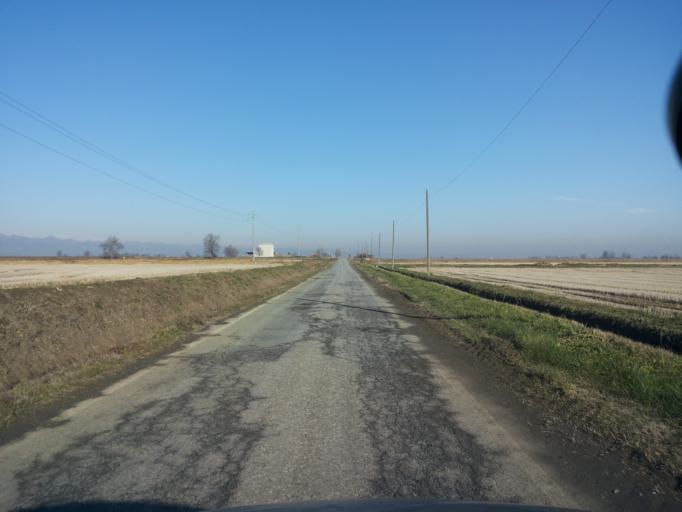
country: IT
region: Piedmont
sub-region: Provincia di Vercelli
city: Formigliana
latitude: 45.4151
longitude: 8.2497
